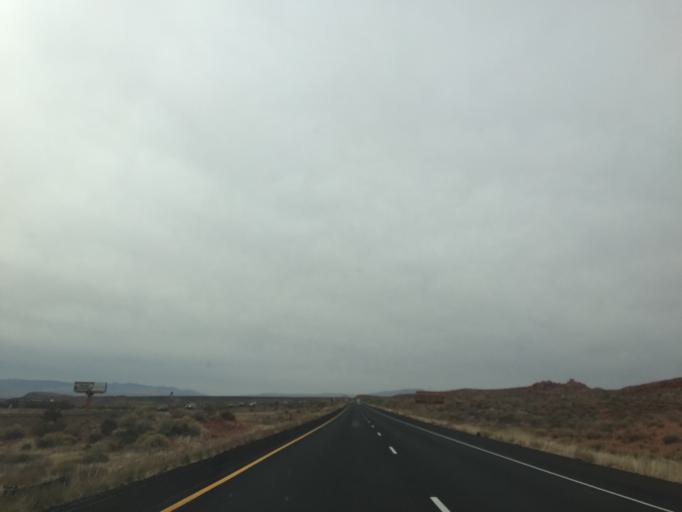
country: US
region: Utah
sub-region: Washington County
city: Washington
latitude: 37.1731
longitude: -113.4370
